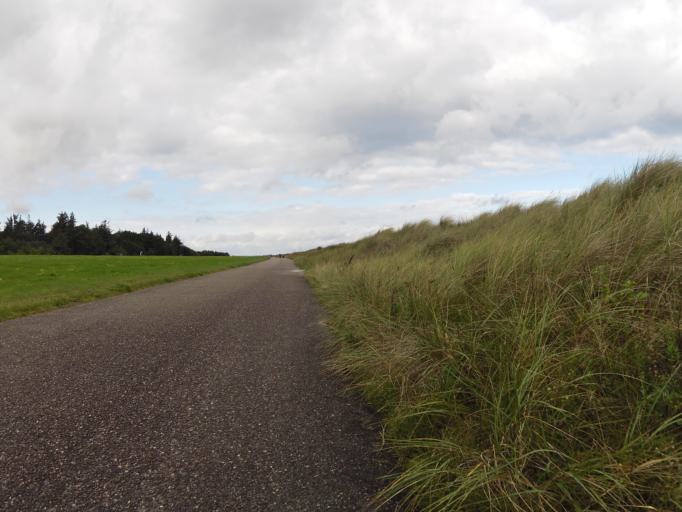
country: DE
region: Schleswig-Holstein
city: Wisch
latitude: 54.4339
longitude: 10.3415
